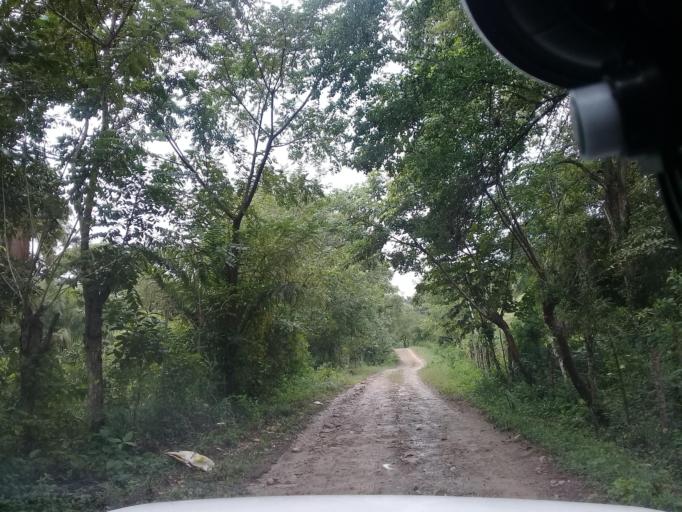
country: MX
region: Veracruz
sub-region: Chalma
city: San Pedro Coyutla
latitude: 21.2378
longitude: -98.4282
